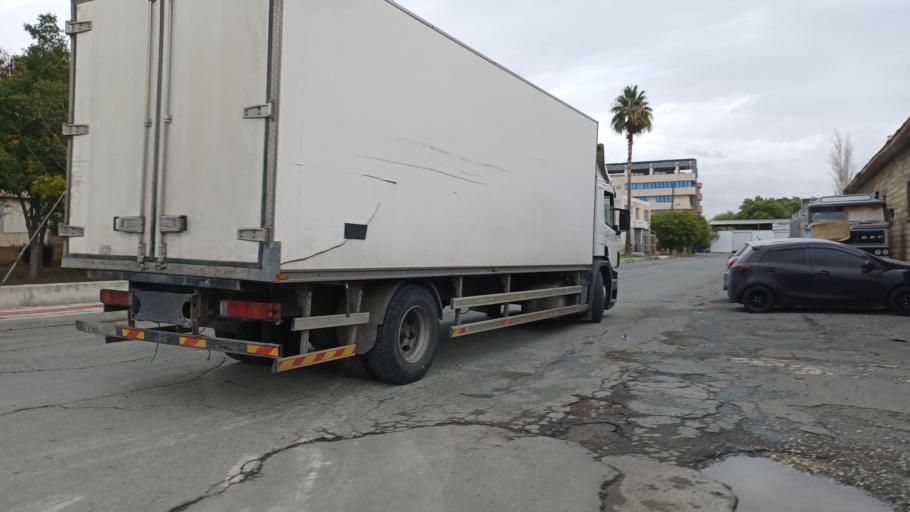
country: CY
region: Limassol
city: Limassol
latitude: 34.6642
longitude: 33.0250
